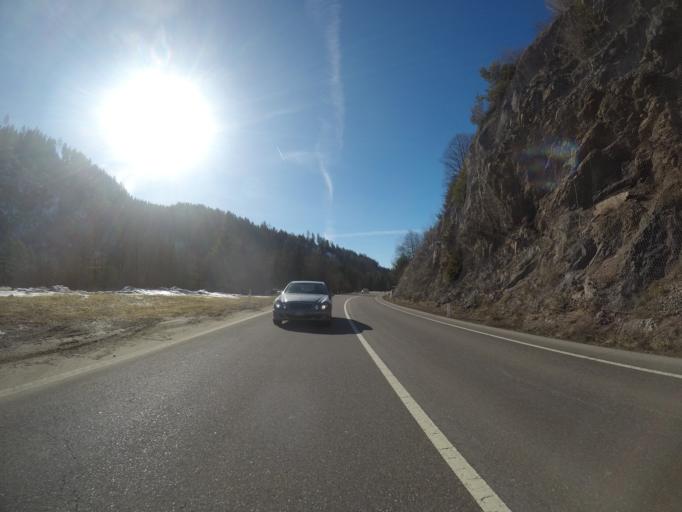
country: IT
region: Trentino-Alto Adige
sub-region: Provincia di Trento
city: Cavalese
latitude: 46.2808
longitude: 11.4601
